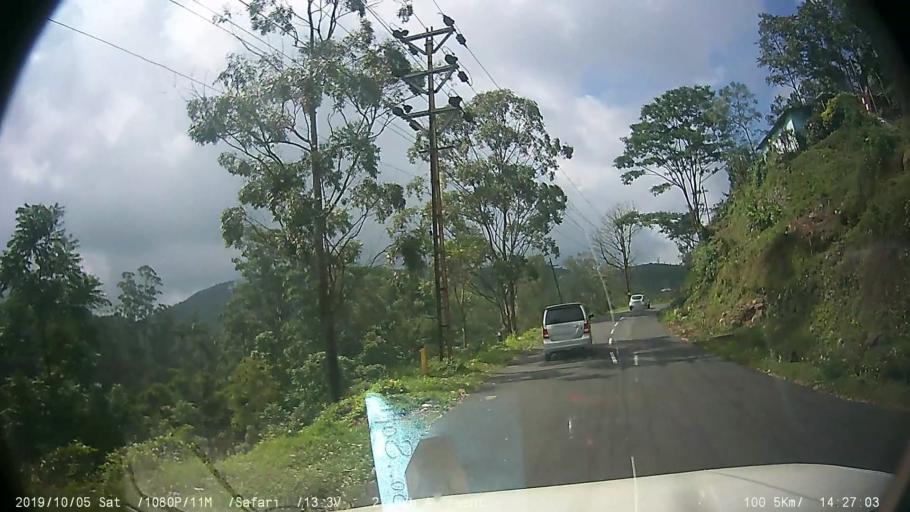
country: IN
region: Kerala
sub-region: Kottayam
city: Erattupetta
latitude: 9.6013
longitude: 76.9666
